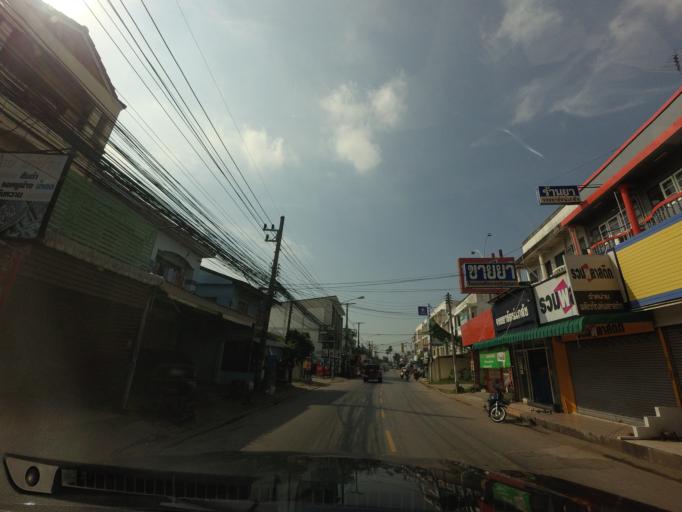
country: TH
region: Khon Kaen
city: Khon Kaen
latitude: 16.4194
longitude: 102.8498
